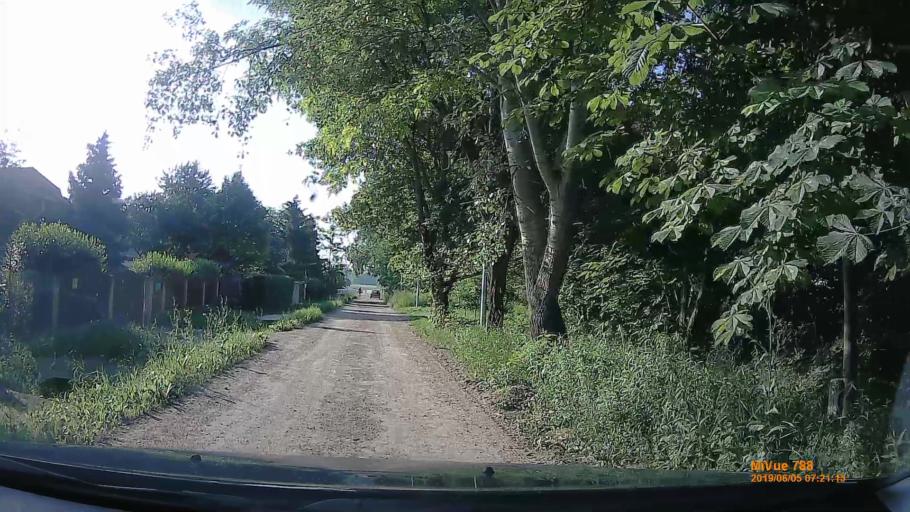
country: HU
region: Pest
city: Urom
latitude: 47.5802
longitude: 19.0298
